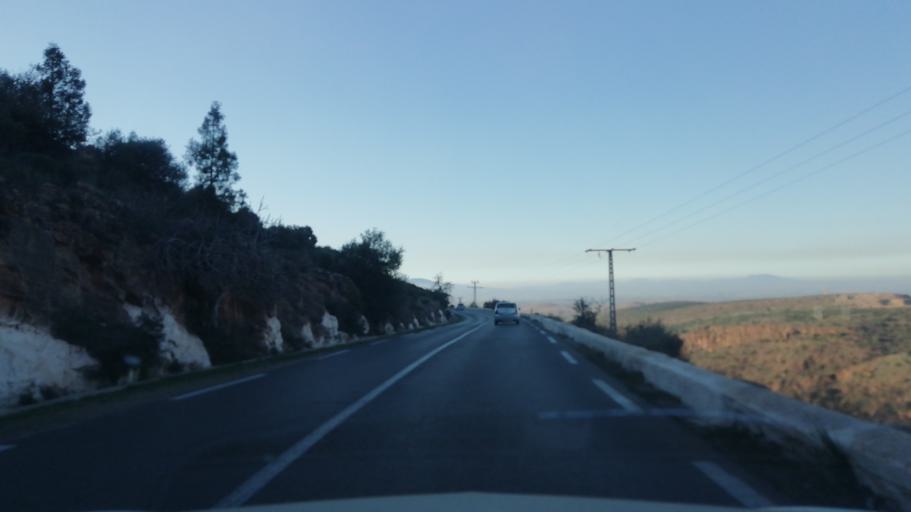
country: DZ
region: Tlemcen
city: Beni Mester
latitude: 34.8498
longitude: -1.4533
